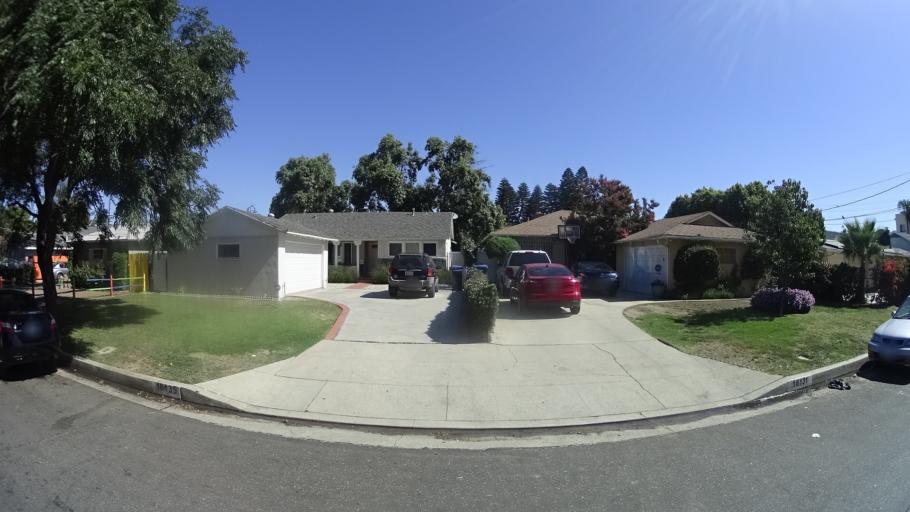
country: US
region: California
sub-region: Los Angeles County
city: Van Nuys
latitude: 34.1902
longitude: -118.4848
